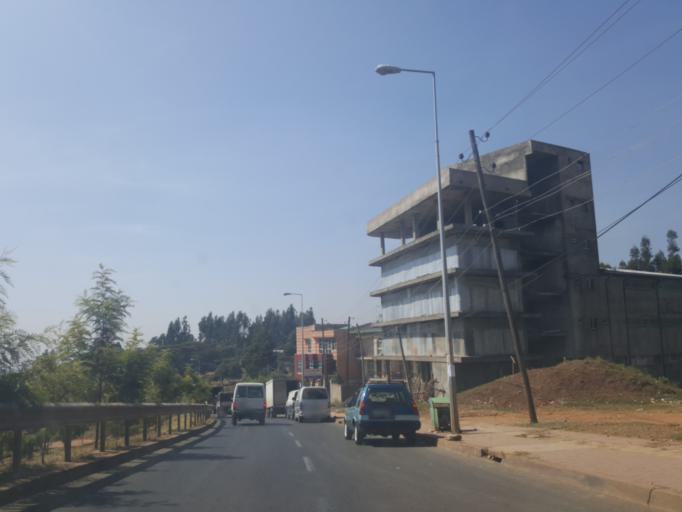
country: ET
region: Adis Abeba
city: Addis Ababa
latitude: 9.0677
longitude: 38.7155
